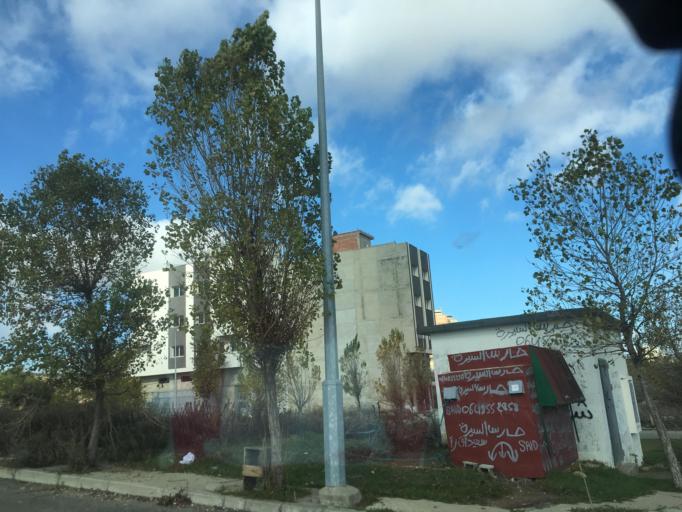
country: MA
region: Tanger-Tetouan
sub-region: Tanger-Assilah
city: Tangier
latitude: 35.7087
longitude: -5.8164
